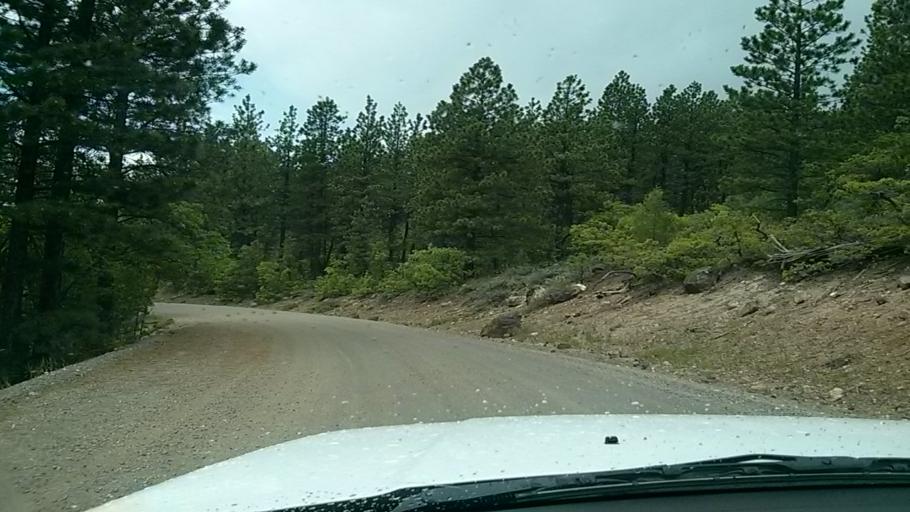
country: US
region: Utah
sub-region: Wayne County
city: Loa
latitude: 37.9473
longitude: -111.6572
